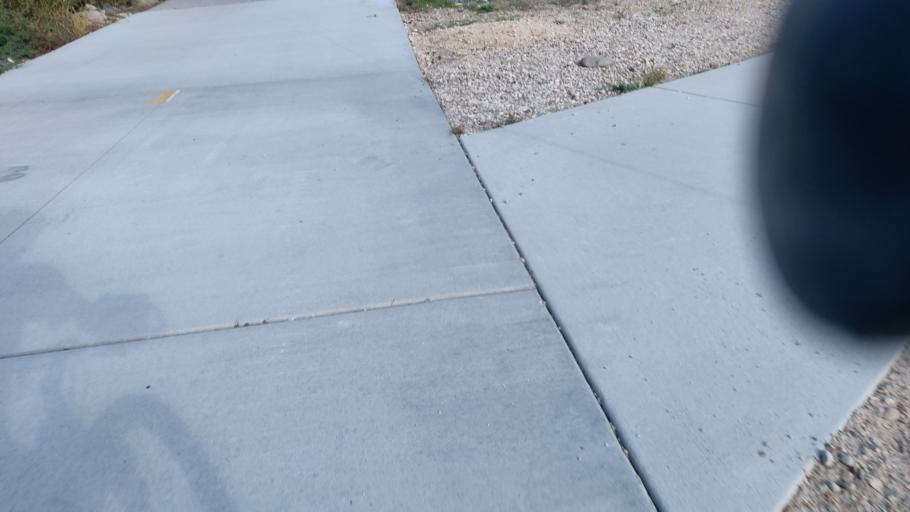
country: US
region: Idaho
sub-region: Ada County
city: Boise
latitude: 43.5717
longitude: -116.1380
